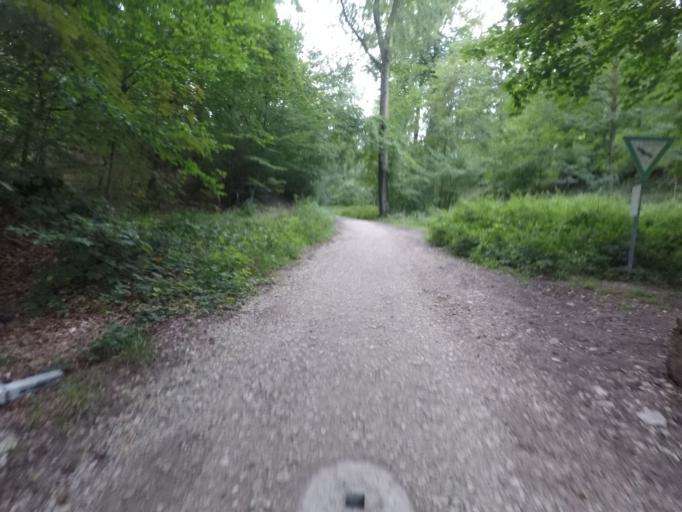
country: DE
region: North Rhine-Westphalia
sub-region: Regierungsbezirk Detmold
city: Bielefeld
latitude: 52.0322
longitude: 8.4949
